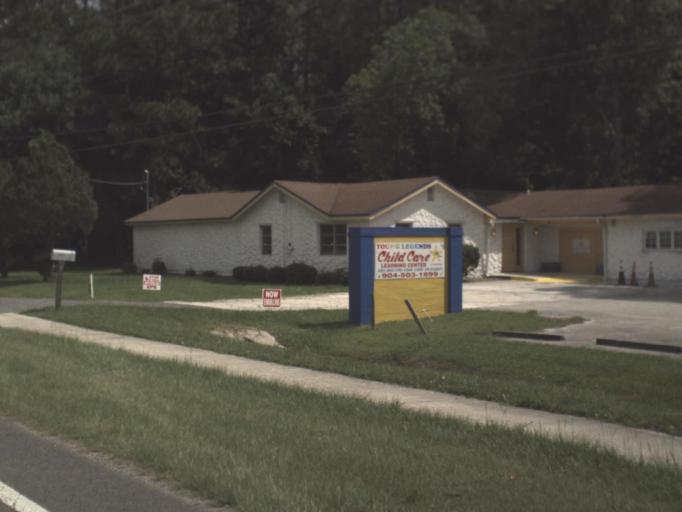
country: US
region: Florida
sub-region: Duval County
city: Jacksonville
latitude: 30.3905
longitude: -81.7352
